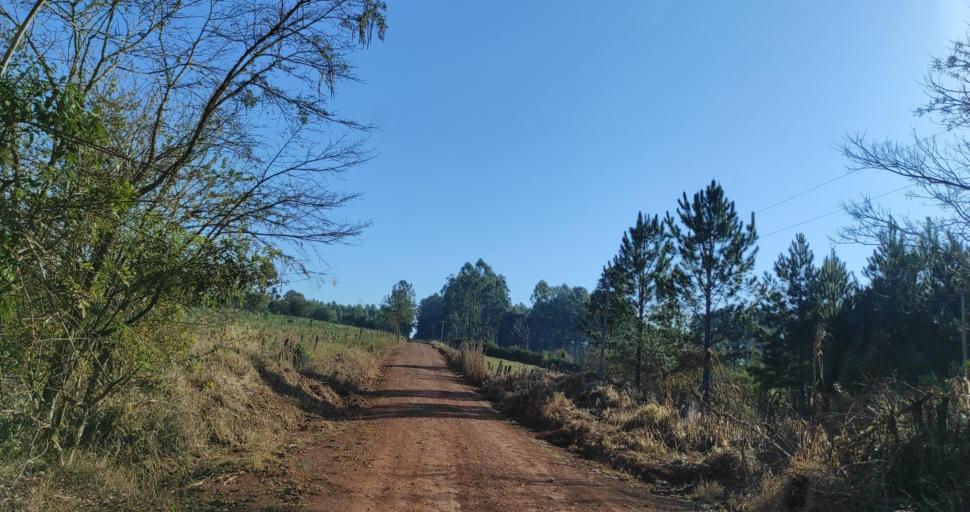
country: AR
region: Misiones
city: Puerto Rico
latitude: -26.8688
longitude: -55.0155
